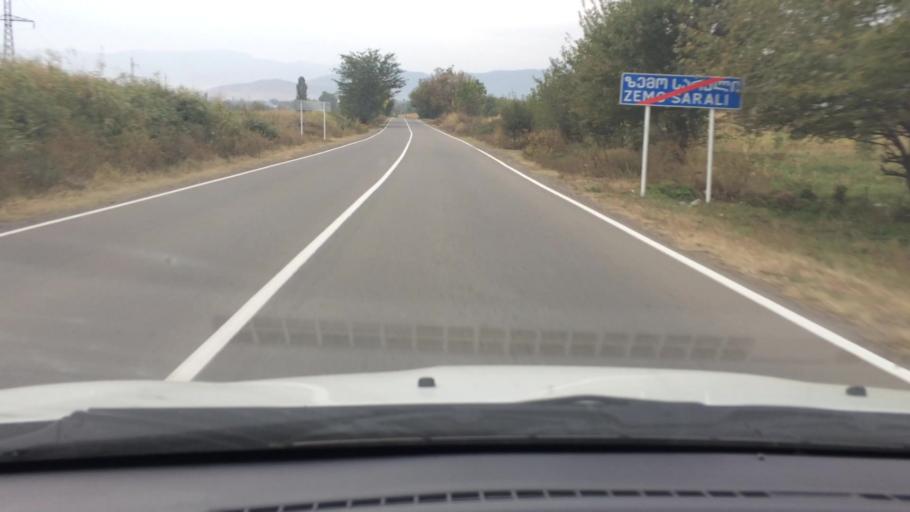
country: GE
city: Naghvarevi
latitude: 41.3203
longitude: 44.7962
